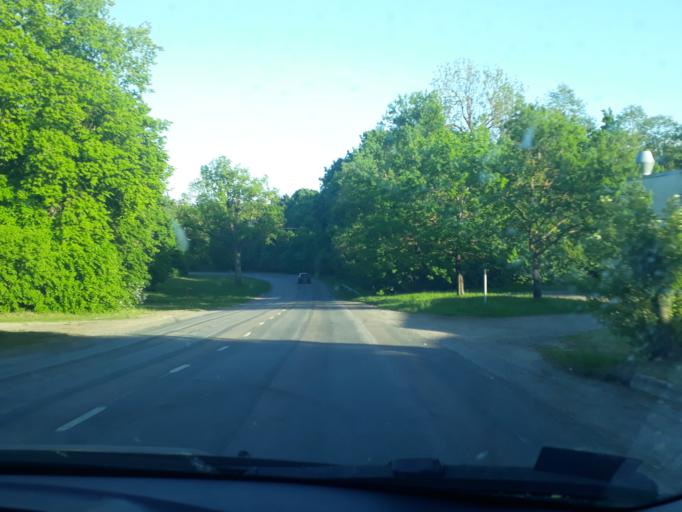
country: EE
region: Paernumaa
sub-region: Paernu linn
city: Parnu
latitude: 58.3873
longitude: 24.5319
